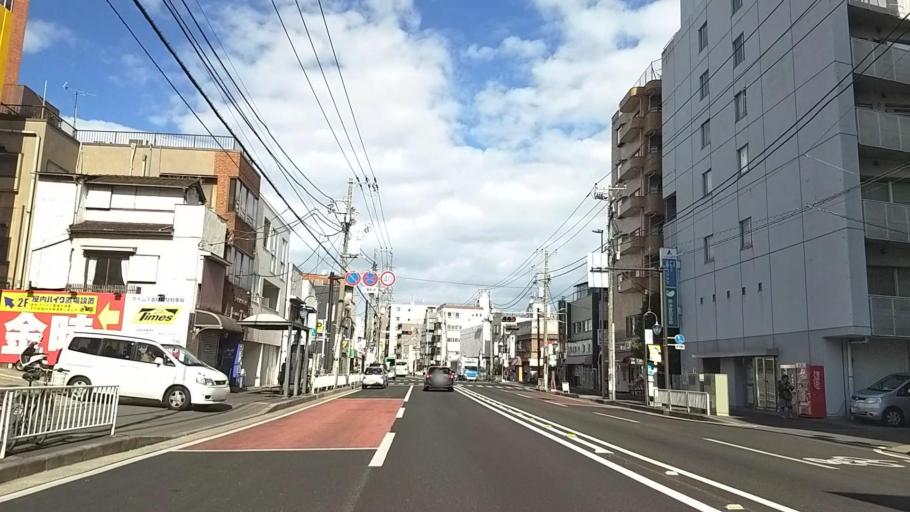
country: JP
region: Kanagawa
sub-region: Kawasaki-shi
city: Kawasaki
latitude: 35.5140
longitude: 139.6743
